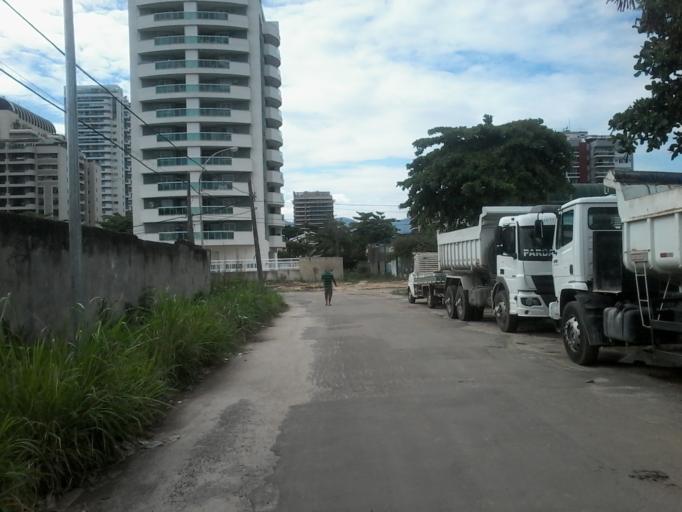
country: BR
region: Rio de Janeiro
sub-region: Nilopolis
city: Nilopolis
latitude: -23.0246
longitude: -43.4845
